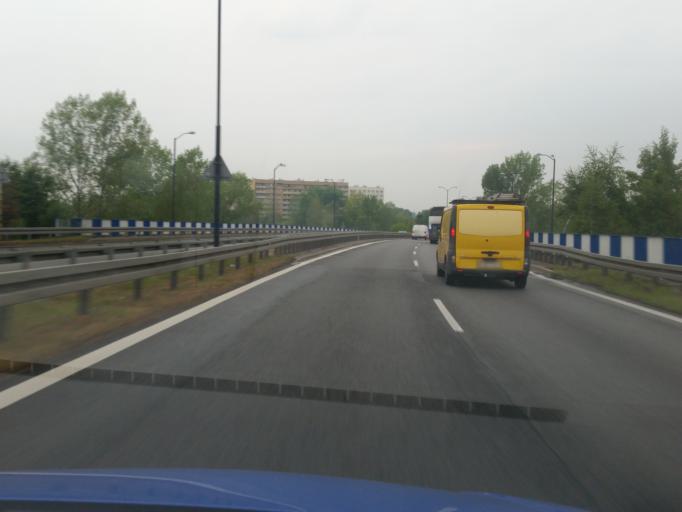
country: PL
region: Silesian Voivodeship
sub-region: Katowice
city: Katowice
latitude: 50.2594
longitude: 19.0680
